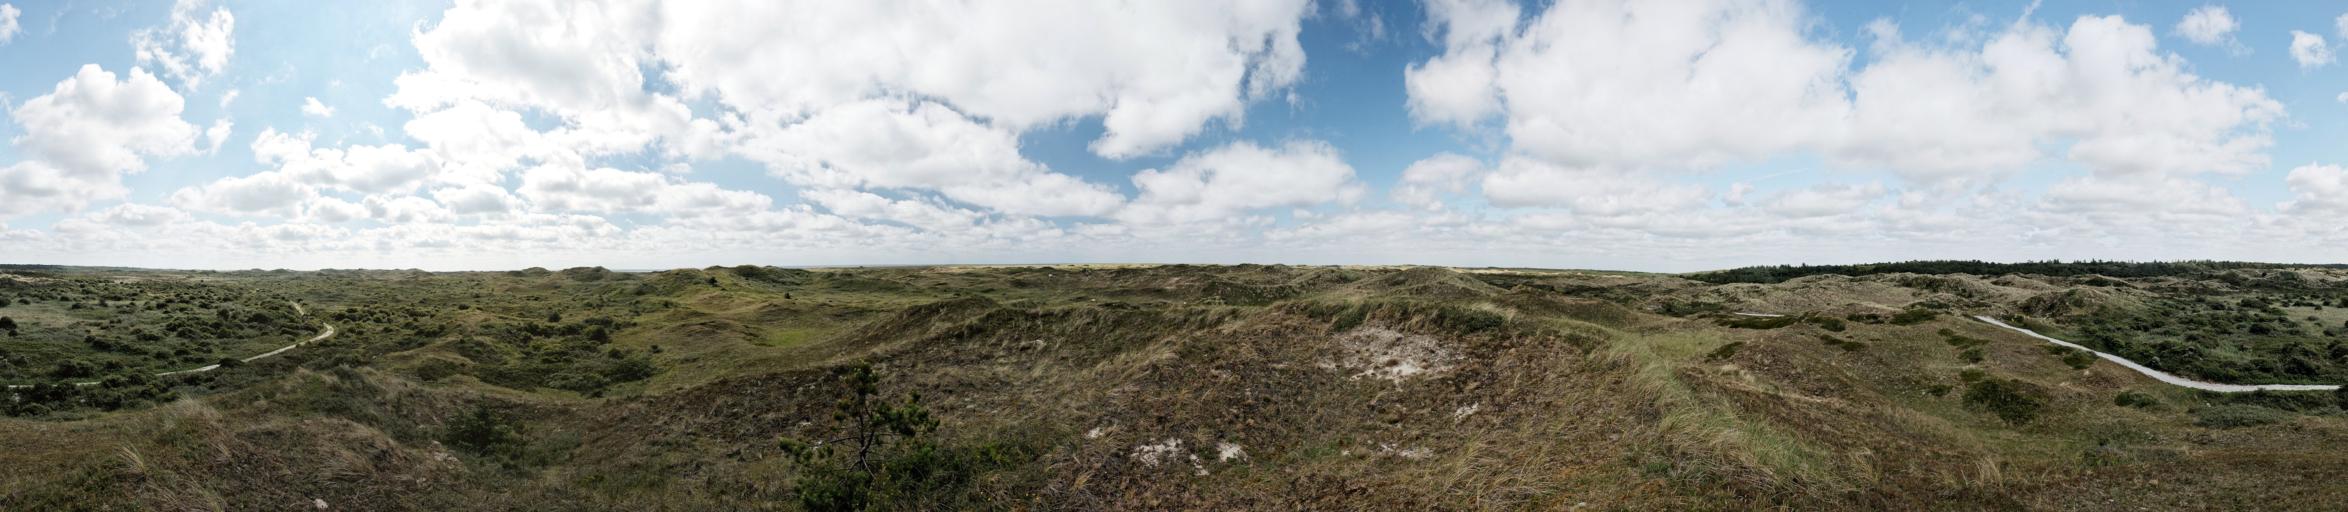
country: NL
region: North Holland
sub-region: Gemeente Texel
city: Den Burg
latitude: 53.0711
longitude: 4.7359
